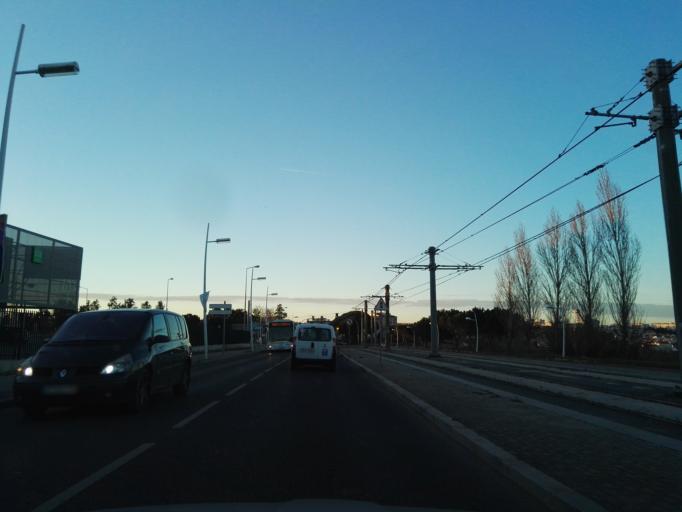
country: PT
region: Setubal
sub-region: Seixal
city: Corroios
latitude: 38.6370
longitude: -9.1471
